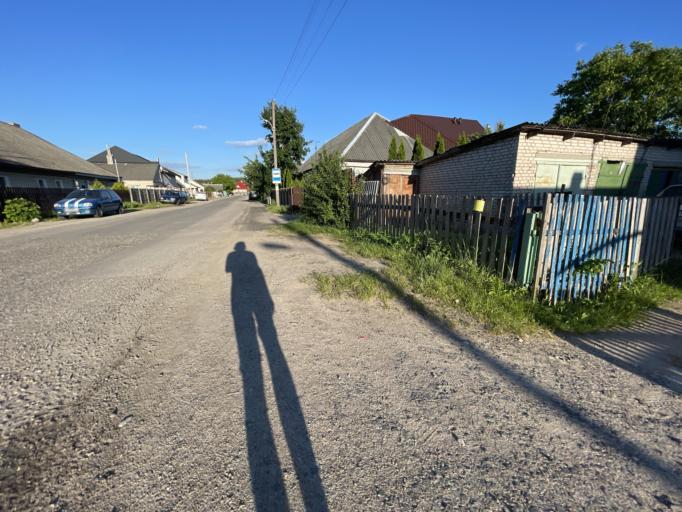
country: BY
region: Grodnenskaya
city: Hrodna
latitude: 53.6508
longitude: 23.8123
